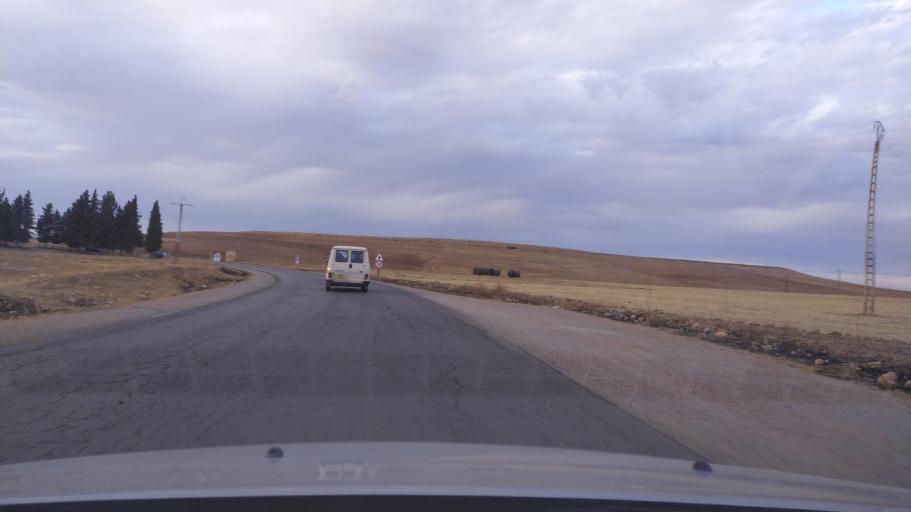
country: DZ
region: Tiaret
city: Frenda
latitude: 35.0251
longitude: 1.0990
